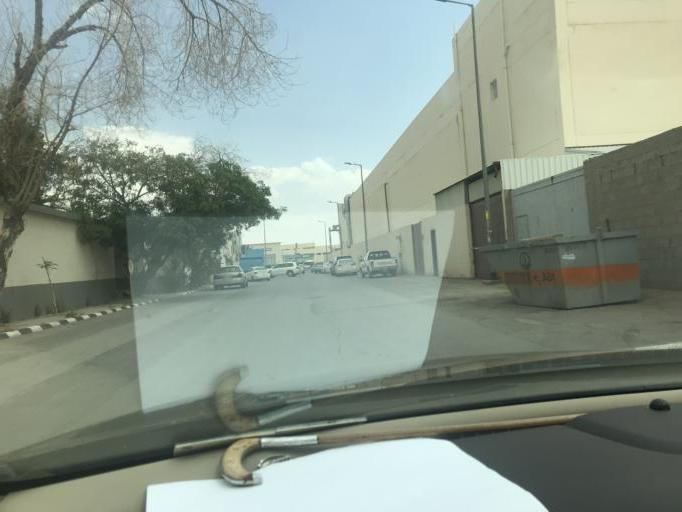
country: SA
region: Ar Riyad
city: Riyadh
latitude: 24.7292
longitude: 46.7817
